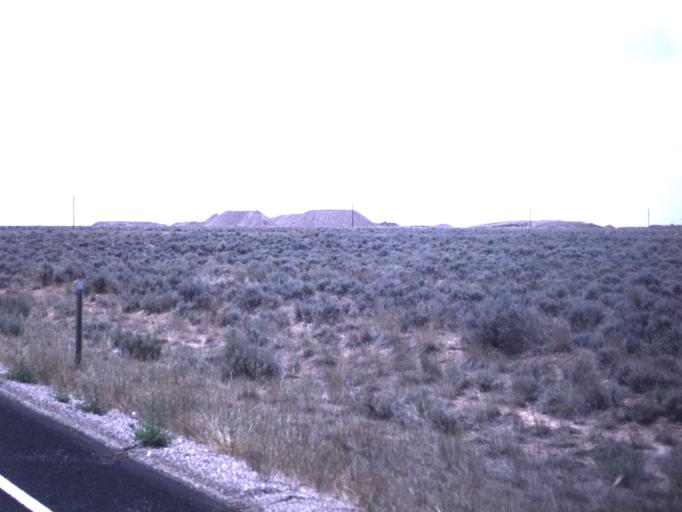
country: US
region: Utah
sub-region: Uintah County
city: Maeser
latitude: 40.4085
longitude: -109.7648
